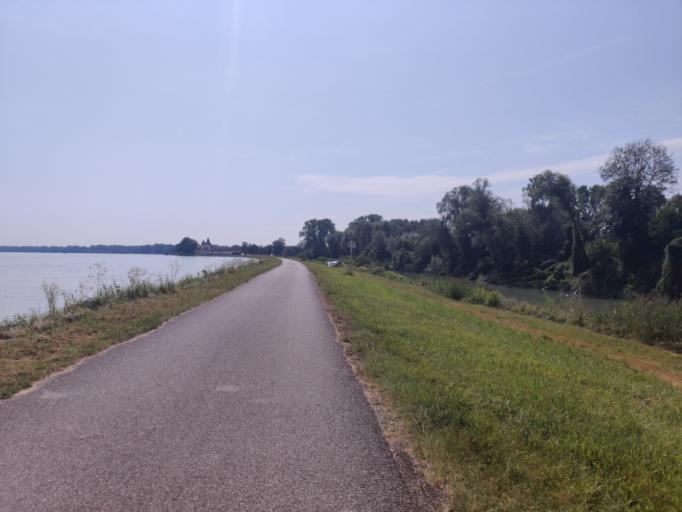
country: AT
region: Upper Austria
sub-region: Politischer Bezirk Urfahr-Umgebung
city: Feldkirchen an der Donau
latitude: 48.3417
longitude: 14.0210
